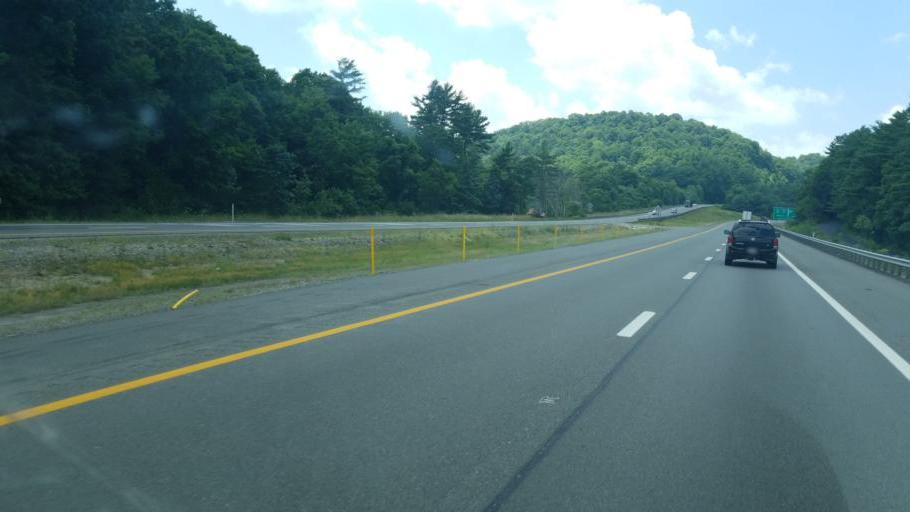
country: US
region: West Virginia
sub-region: Raleigh County
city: Beaver
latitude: 37.7182
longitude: -81.1575
